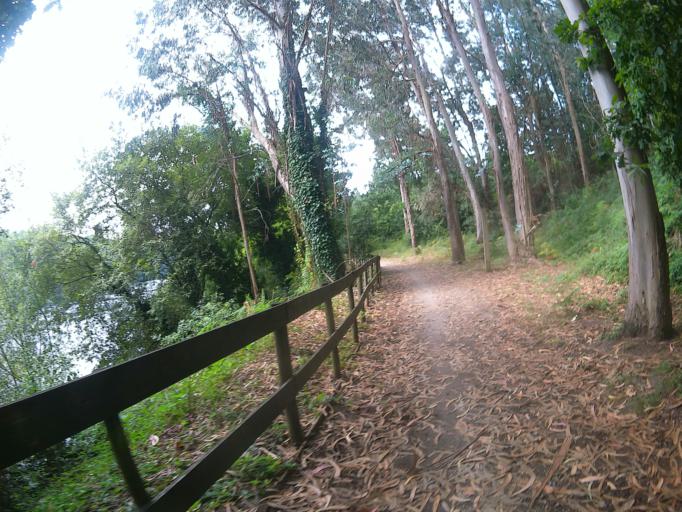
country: PT
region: Viana do Castelo
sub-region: Ponte de Lima
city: Ponte de Lima
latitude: 41.7779
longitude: -8.5550
